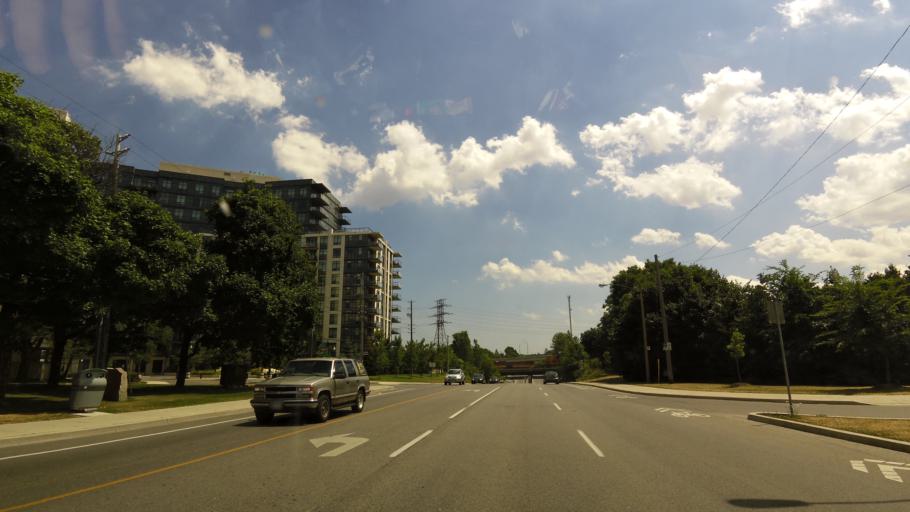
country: CA
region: Ontario
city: Etobicoke
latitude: 43.6608
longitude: -79.5174
